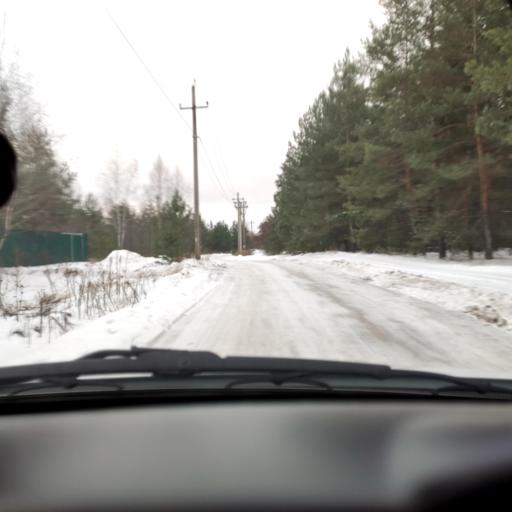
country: RU
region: Voronezj
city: Ramon'
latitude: 51.8858
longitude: 39.2562
